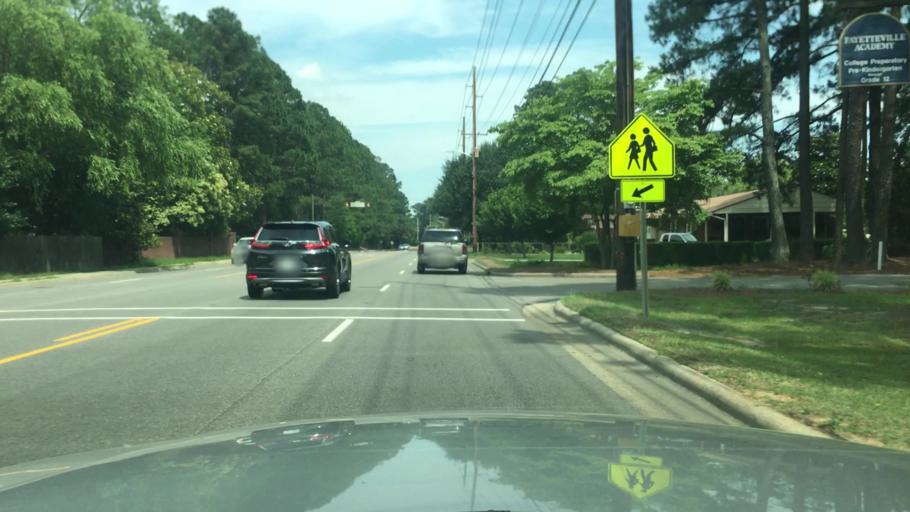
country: US
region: North Carolina
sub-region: Cumberland County
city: Fayetteville
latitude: 35.0650
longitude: -78.9403
